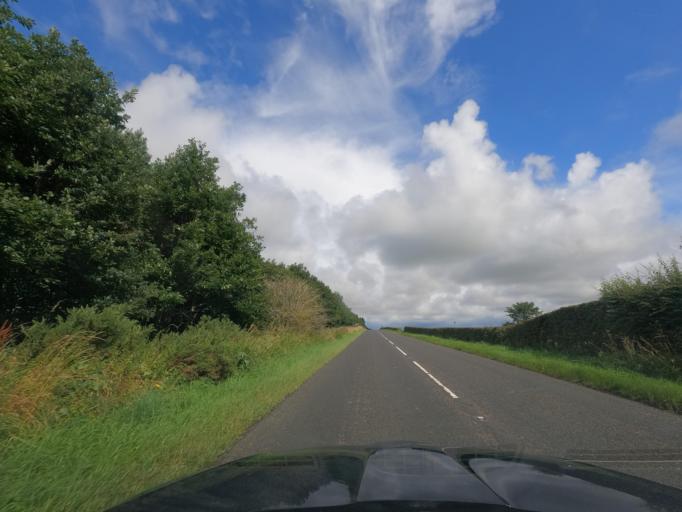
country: GB
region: England
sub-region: Northumberland
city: Lowick
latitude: 55.6106
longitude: -1.9997
